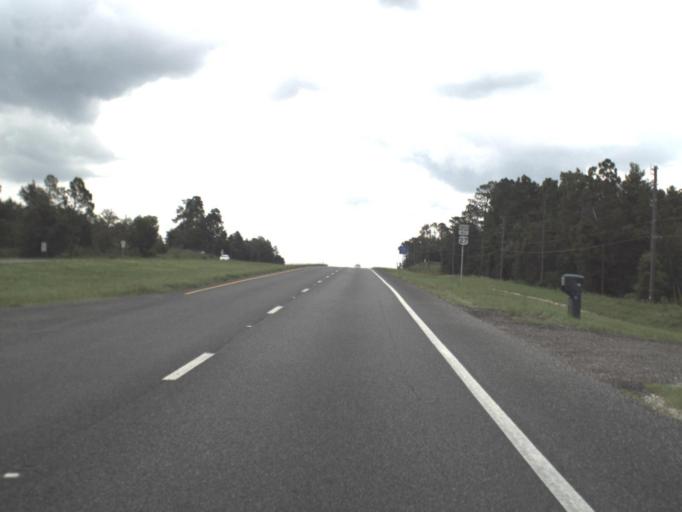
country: US
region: Florida
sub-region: Levy County
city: East Bronson
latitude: 29.4273
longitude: -82.5960
